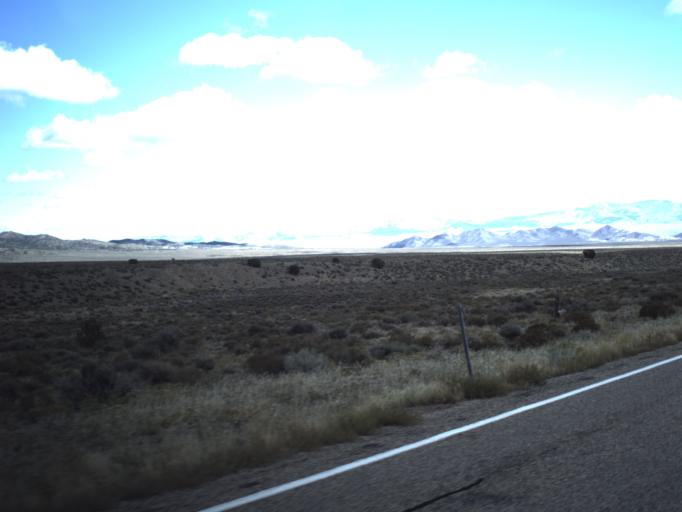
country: US
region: Utah
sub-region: Beaver County
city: Milford
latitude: 38.4542
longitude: -113.2109
